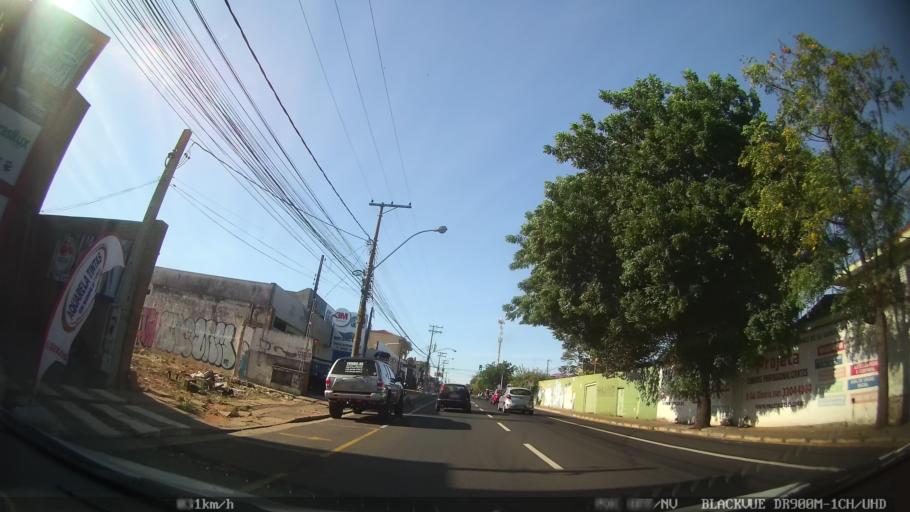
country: BR
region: Sao Paulo
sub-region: Sao Jose Do Rio Preto
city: Sao Jose do Rio Preto
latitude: -20.8018
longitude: -49.3707
